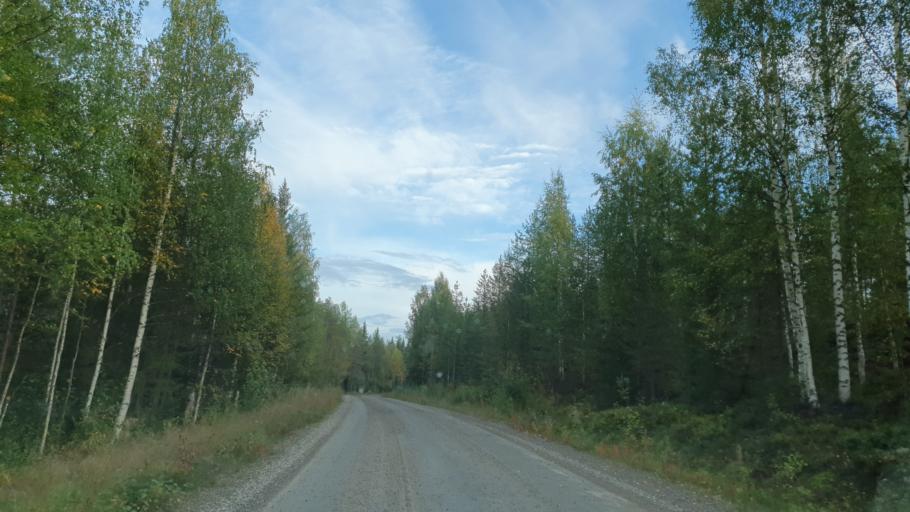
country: FI
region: Kainuu
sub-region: Kehys-Kainuu
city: Kuhmo
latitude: 64.4043
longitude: 29.5538
